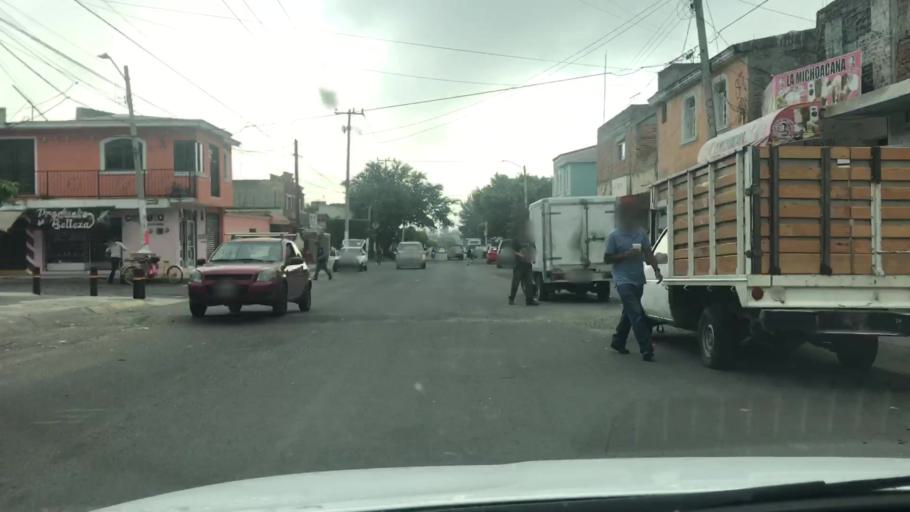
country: MX
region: Jalisco
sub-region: Tlajomulco de Zuniga
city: Palomar
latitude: 20.6404
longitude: -103.4509
